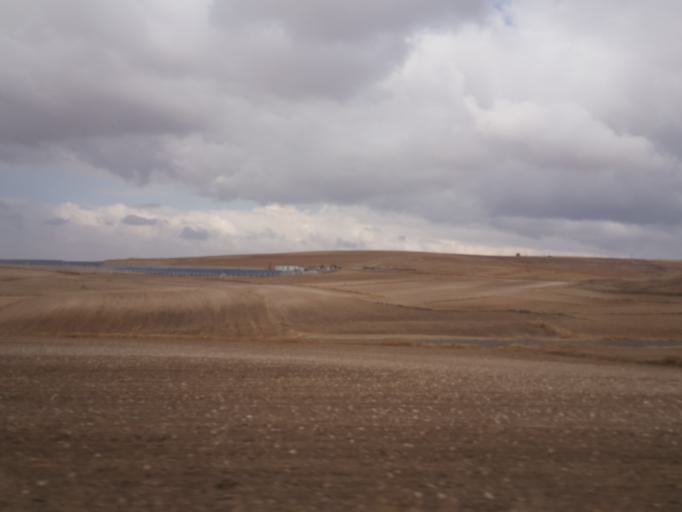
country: TR
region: Kirikkale
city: Keskin
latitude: 39.6419
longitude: 33.6143
